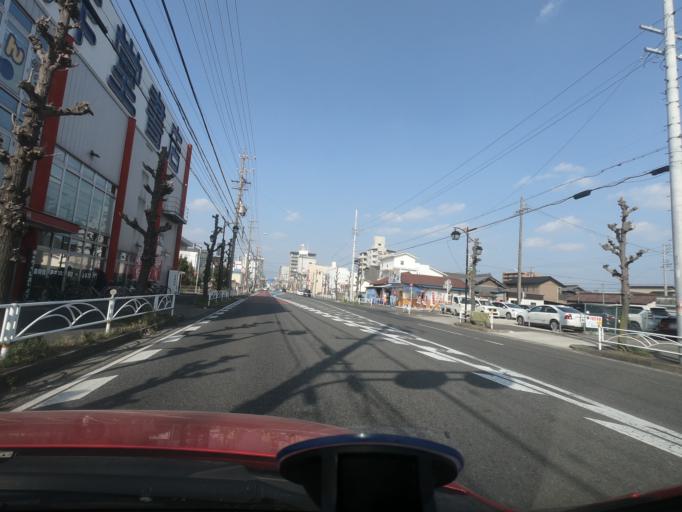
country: JP
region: Aichi
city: Kasugai
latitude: 35.2432
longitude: 136.9709
